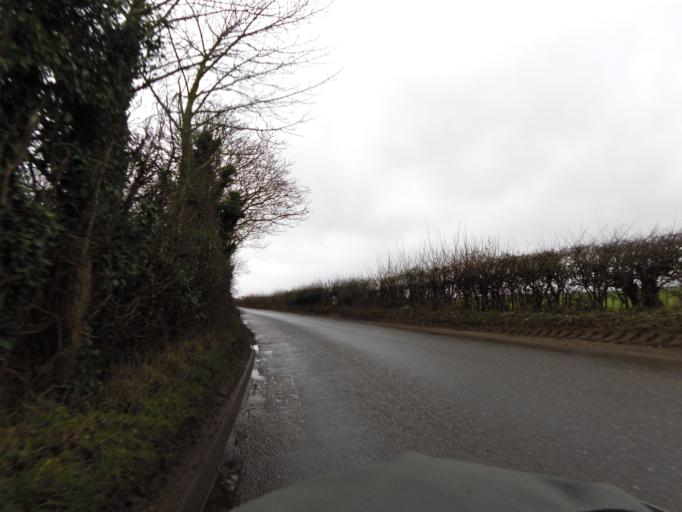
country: GB
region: England
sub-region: Norfolk
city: Briston
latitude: 52.8980
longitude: 1.0886
